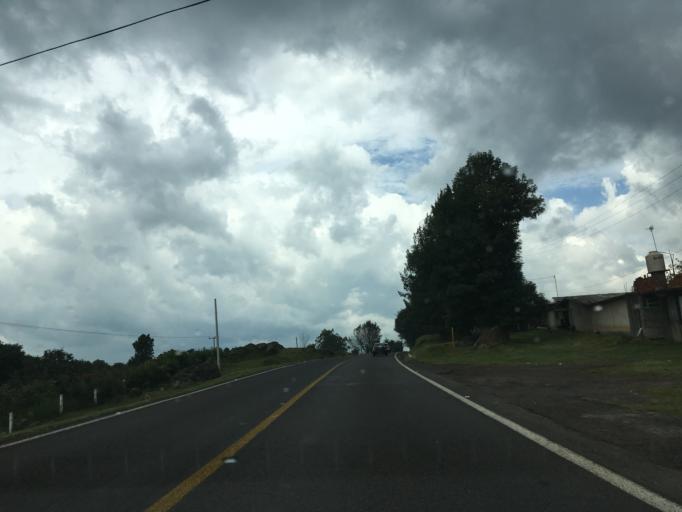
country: MX
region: Michoacan
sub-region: Patzcuaro
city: Santa Ana Chapitiro
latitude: 19.5295
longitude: -101.6402
